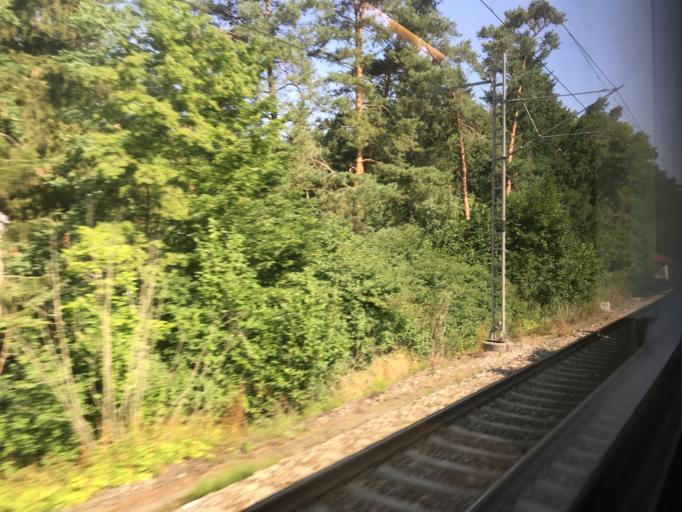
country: CZ
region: Central Bohemia
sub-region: Okres Benesov
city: Cercany
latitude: 49.8864
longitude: 14.7272
